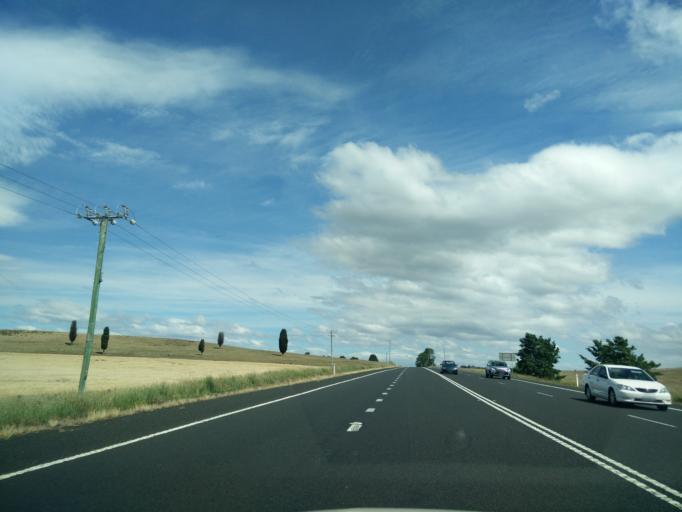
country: AU
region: Tasmania
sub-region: Northern Midlands
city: Evandale
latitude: -41.8764
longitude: 147.4627
